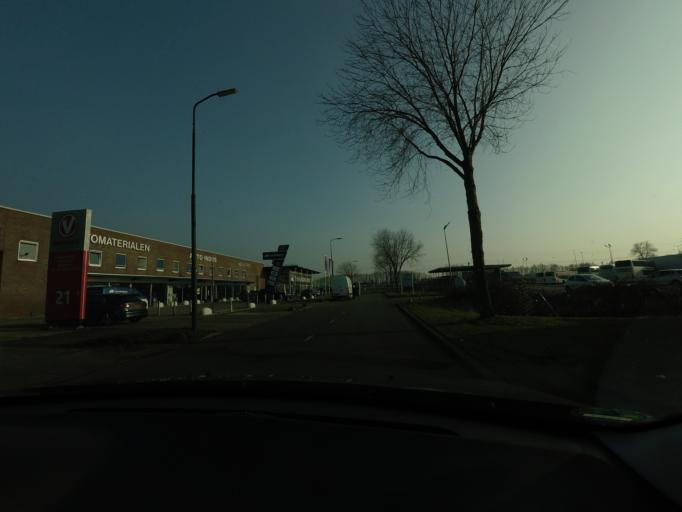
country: NL
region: Utrecht
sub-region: Gemeente Woerden
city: Woerden
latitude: 52.0742
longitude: 4.9037
